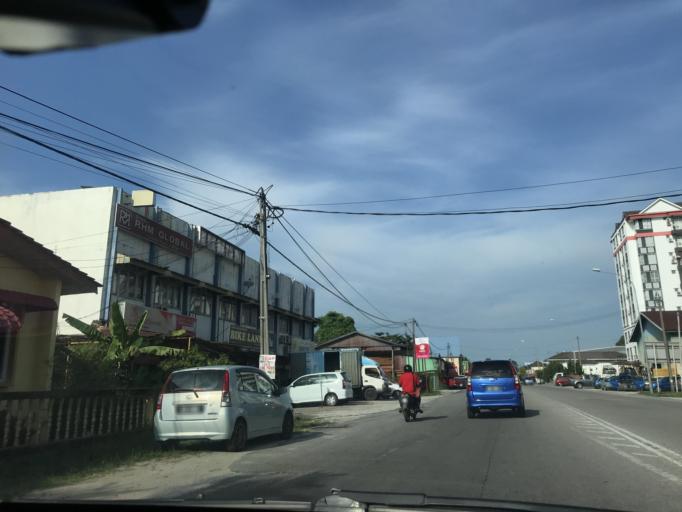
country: MY
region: Kelantan
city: Kota Bharu
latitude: 6.1242
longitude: 102.2734
